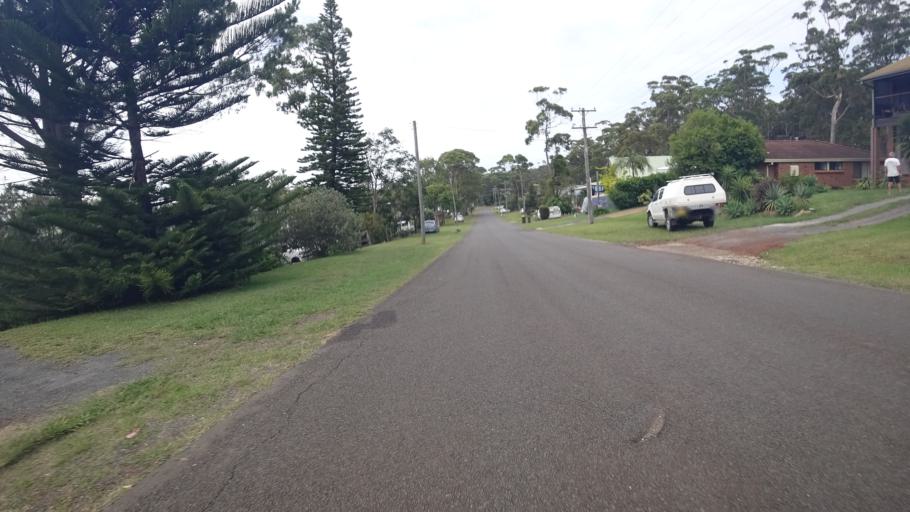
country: AU
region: New South Wales
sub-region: Shoalhaven Shire
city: Milton
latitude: -35.2561
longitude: 150.5134
